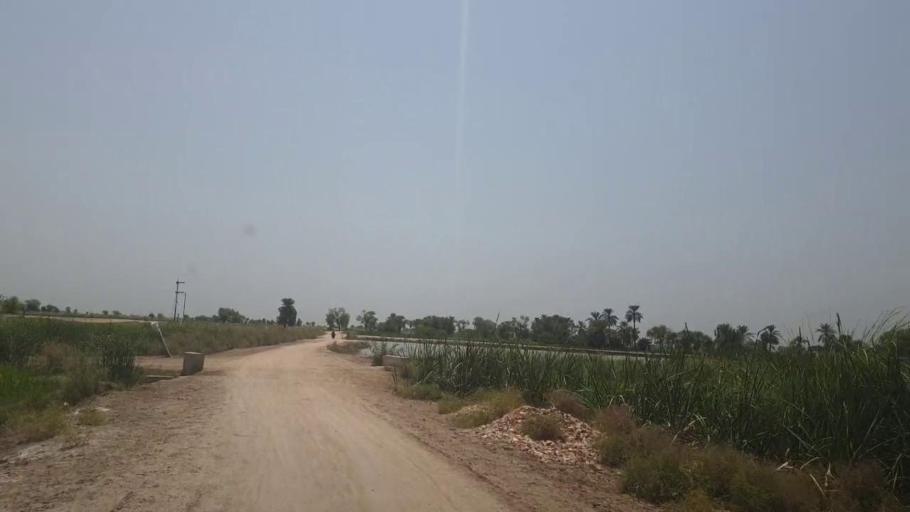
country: PK
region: Sindh
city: Lakhi
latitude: 27.8612
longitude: 68.6638
